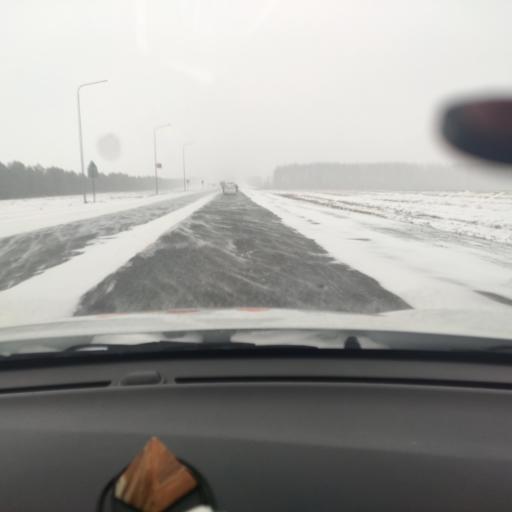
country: RU
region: Tatarstan
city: Verkhniy Uslon
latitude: 55.6614
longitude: 48.8588
